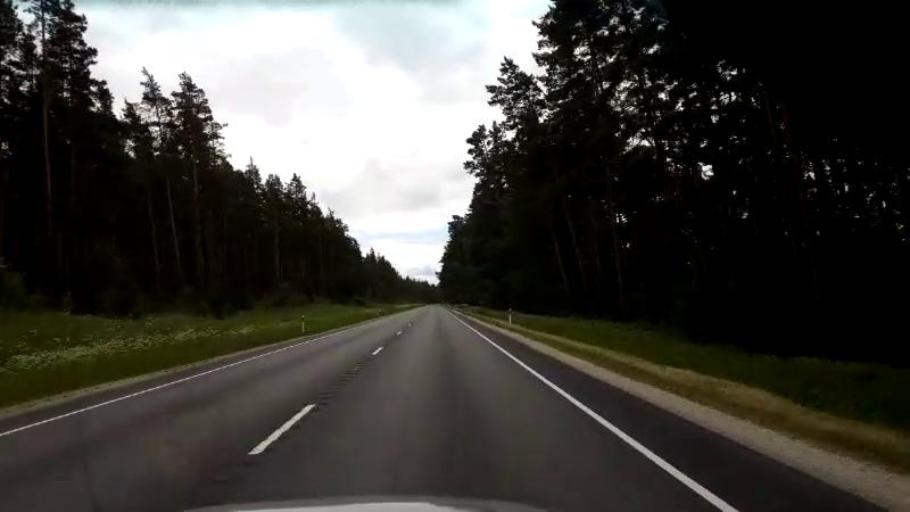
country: EE
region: Paernumaa
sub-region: Paernu linn
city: Parnu
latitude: 58.1580
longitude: 24.4985
